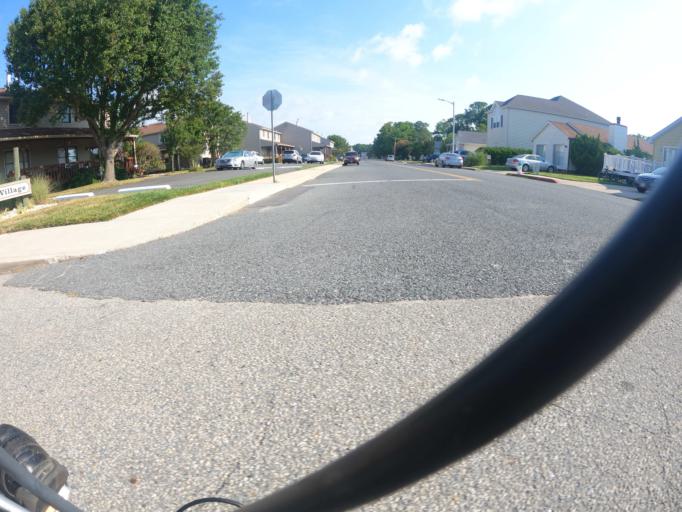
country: US
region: Delaware
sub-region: Sussex County
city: Bethany Beach
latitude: 38.4427
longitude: -75.0590
